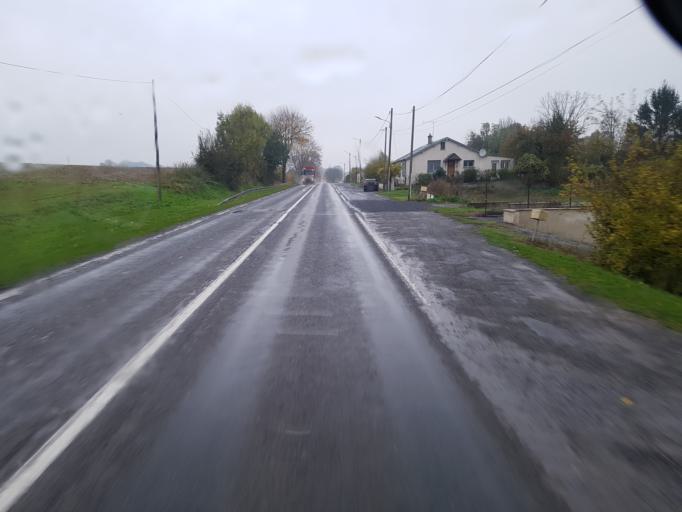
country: FR
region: Picardie
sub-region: Departement de l'Aisne
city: Saint-Quentin
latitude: 49.8672
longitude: 3.2732
